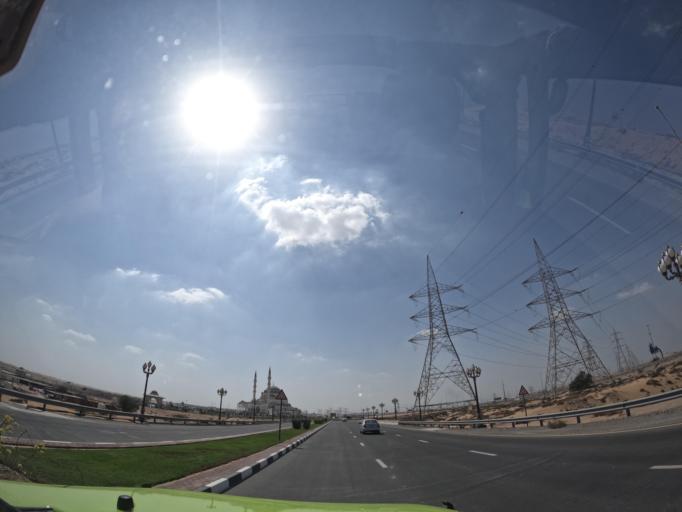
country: AE
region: Ash Shariqah
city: Sharjah
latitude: 25.2453
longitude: 55.5713
